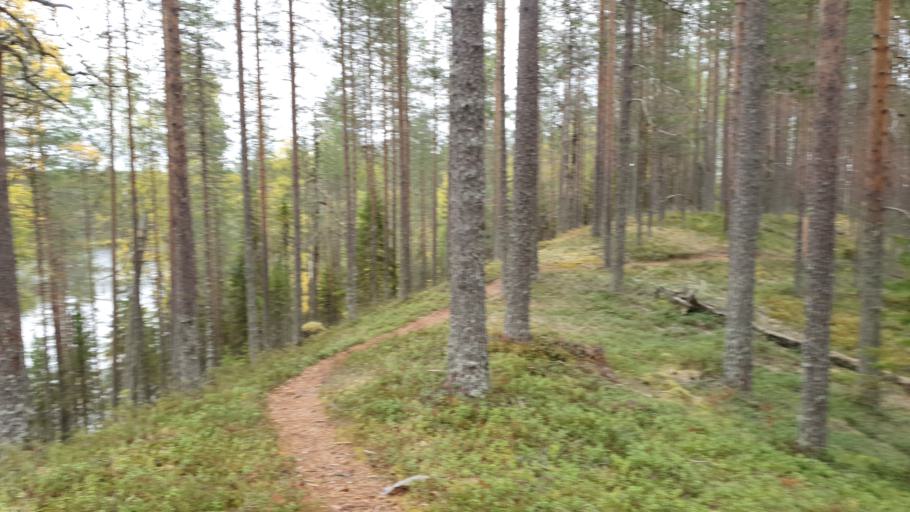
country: FI
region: Kainuu
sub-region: Kehys-Kainuu
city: Kuhmo
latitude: 64.2923
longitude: 29.3274
